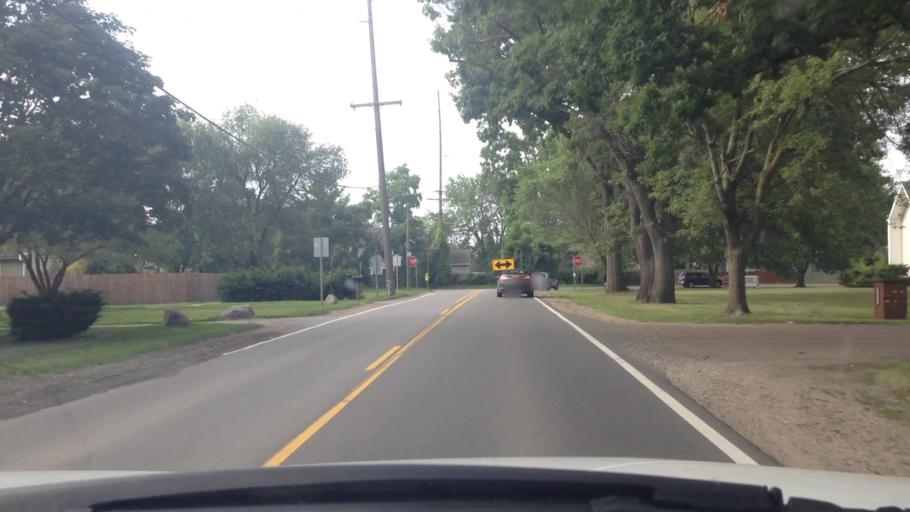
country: US
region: Michigan
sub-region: Oakland County
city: Waterford
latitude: 42.6914
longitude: -83.3483
